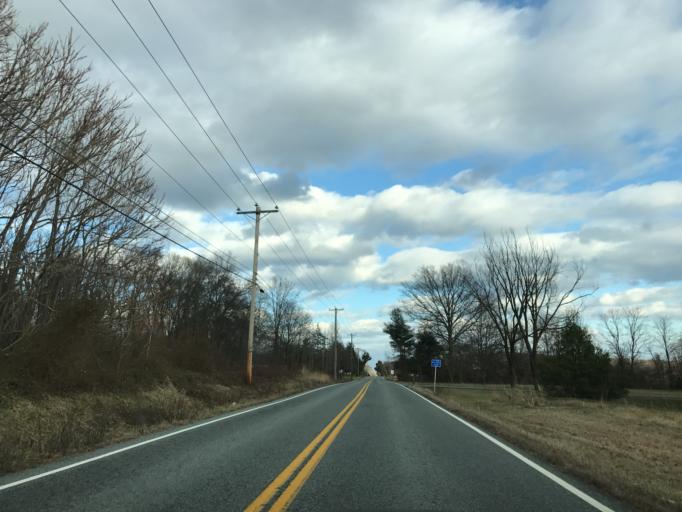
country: US
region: Maryland
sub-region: Cecil County
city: Rising Sun
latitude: 39.6375
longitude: -76.0213
